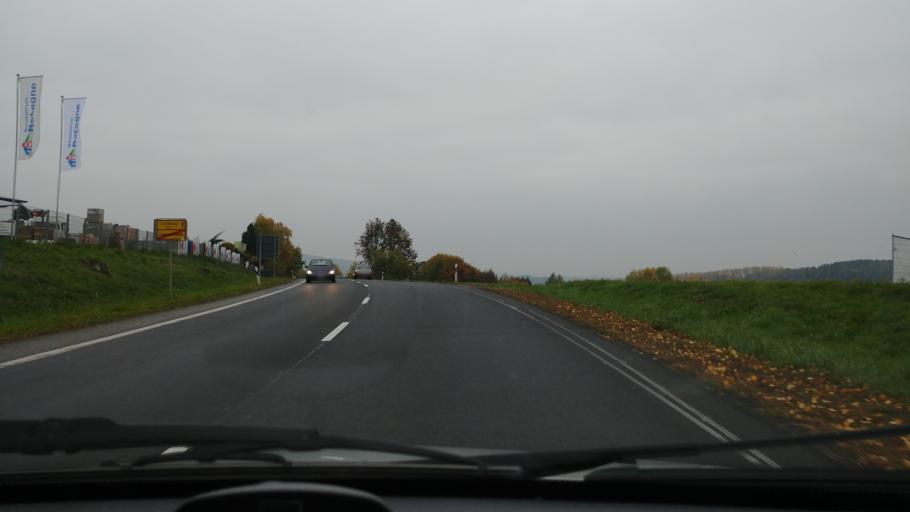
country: DE
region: Rheinland-Pfalz
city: Irmtraut
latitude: 50.5349
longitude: 8.0482
